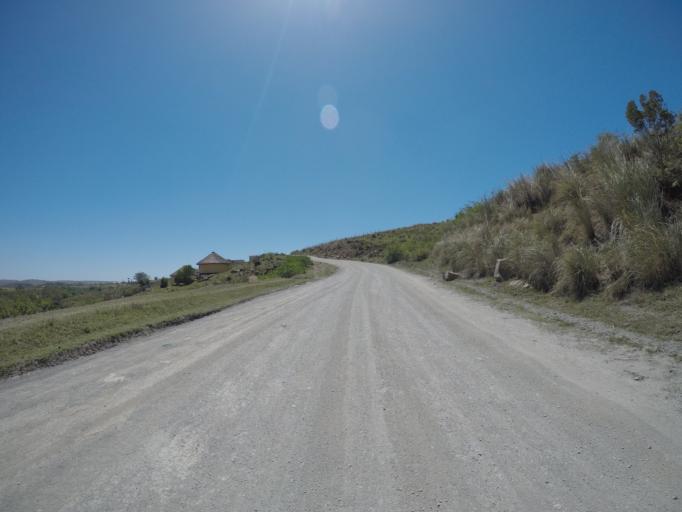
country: ZA
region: Eastern Cape
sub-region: OR Tambo District Municipality
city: Libode
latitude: -32.0112
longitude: 29.0730
